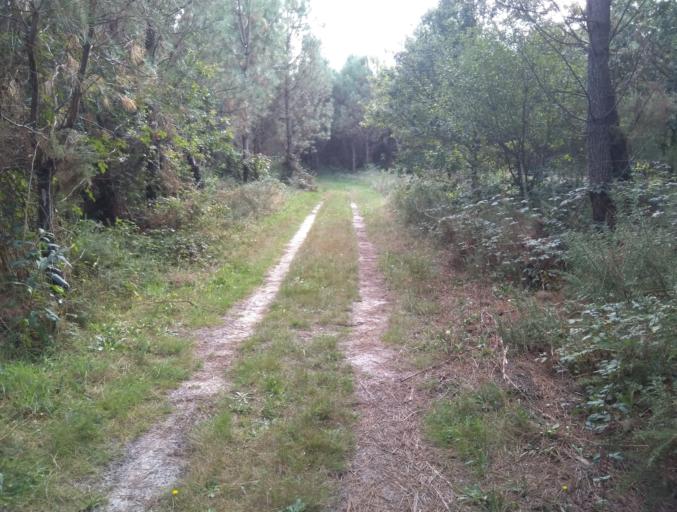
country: FR
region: Aquitaine
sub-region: Departement des Landes
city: Saint-Vincent-de-Paul
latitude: 43.7720
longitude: -0.9876
